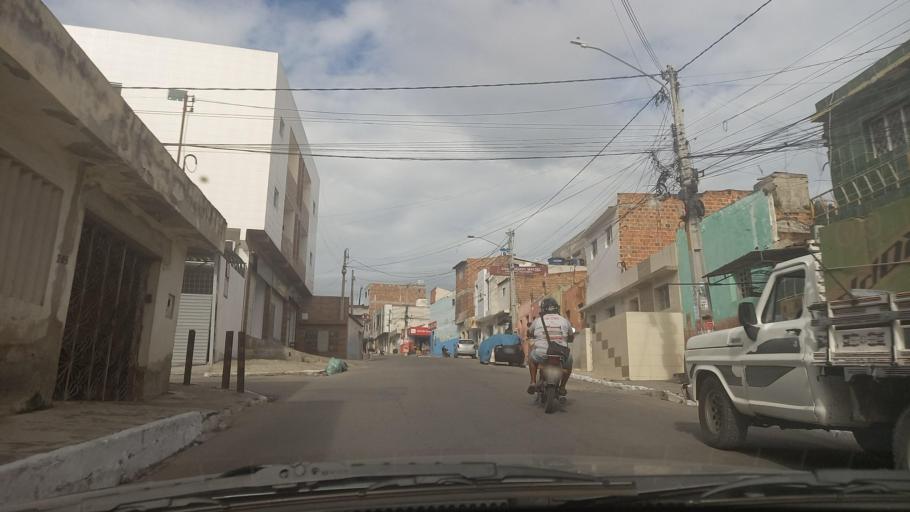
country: BR
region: Pernambuco
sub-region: Caruaru
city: Caruaru
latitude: -8.2858
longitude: -35.9873
